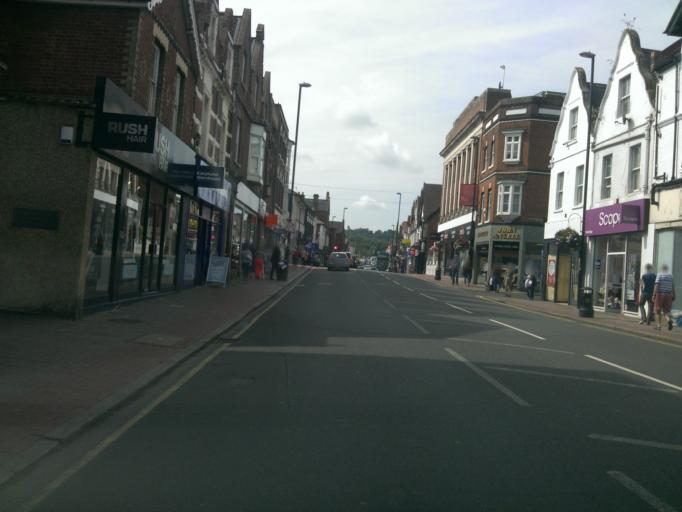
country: GB
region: England
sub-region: Kent
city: Tonbridge
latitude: 51.1944
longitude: 0.2741
